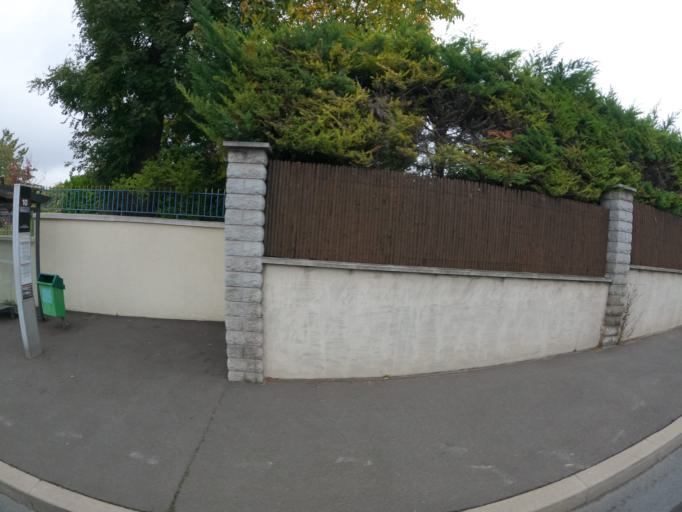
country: FR
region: Ile-de-France
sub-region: Departement du Val-de-Marne
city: Sucy-en-Brie
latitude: 48.7809
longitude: 2.5175
